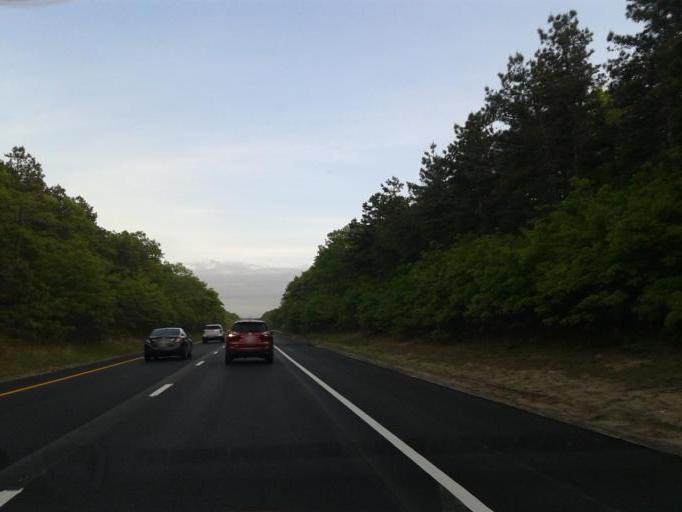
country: US
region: Massachusetts
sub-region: Barnstable County
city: North Falmouth
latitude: 41.6617
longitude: -70.6007
